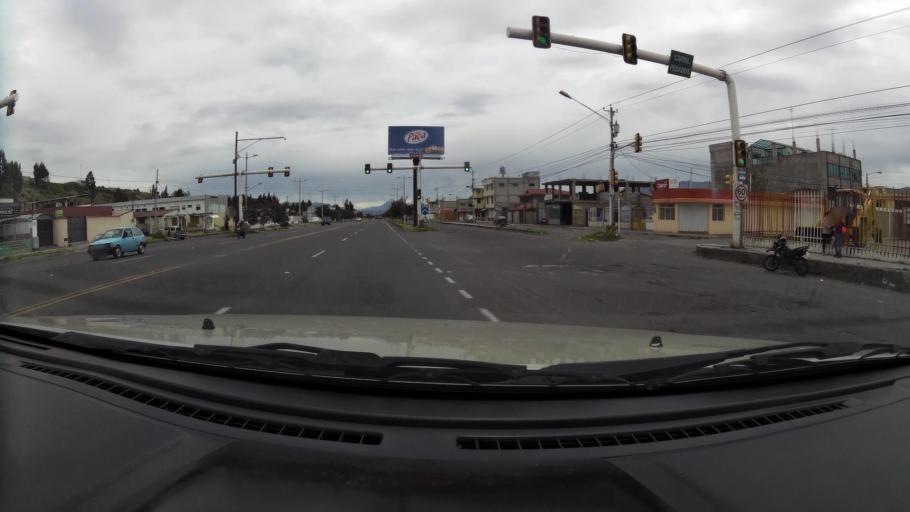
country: EC
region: Cotopaxi
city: Latacunga
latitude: -0.9675
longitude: -78.6143
